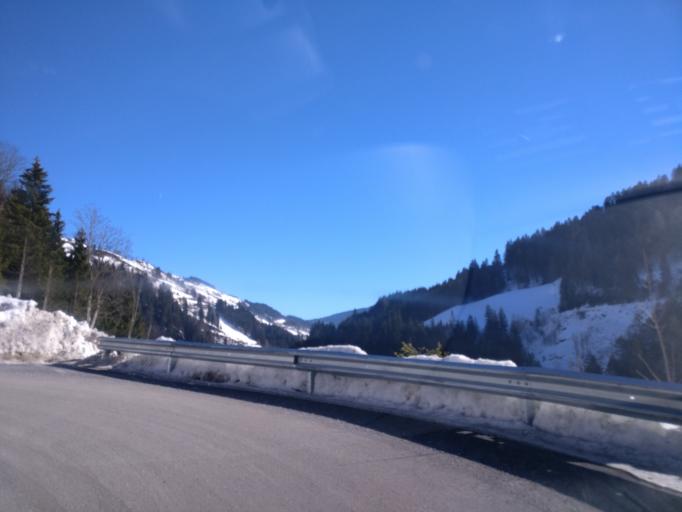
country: AT
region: Salzburg
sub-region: Politischer Bezirk Sankt Johann im Pongau
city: Sankt Johann im Pongau
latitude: 47.3314
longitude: 13.2348
